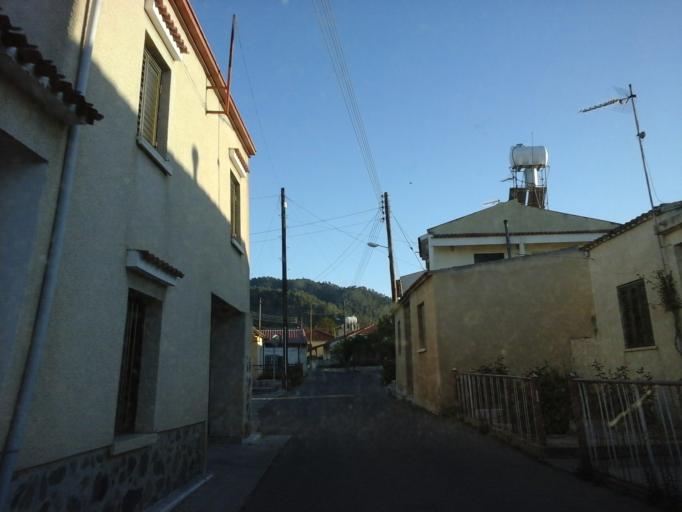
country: CY
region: Lefkosia
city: Astromeritis
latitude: 35.0712
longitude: 32.9922
